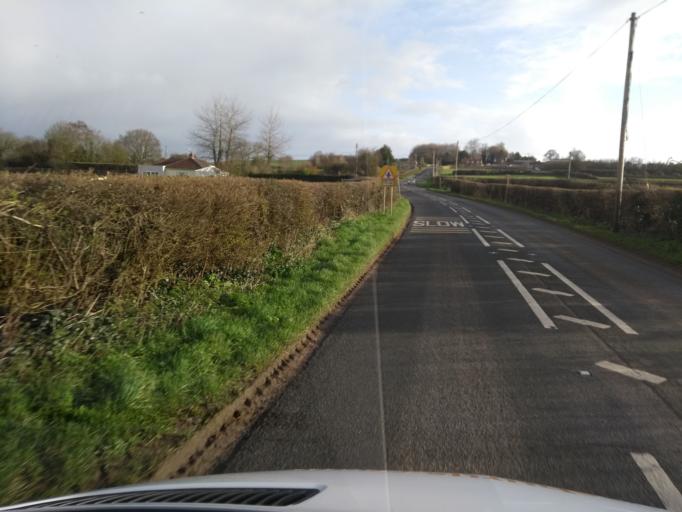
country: GB
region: England
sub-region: Somerset
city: Castle Cary
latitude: 51.0727
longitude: -2.5163
